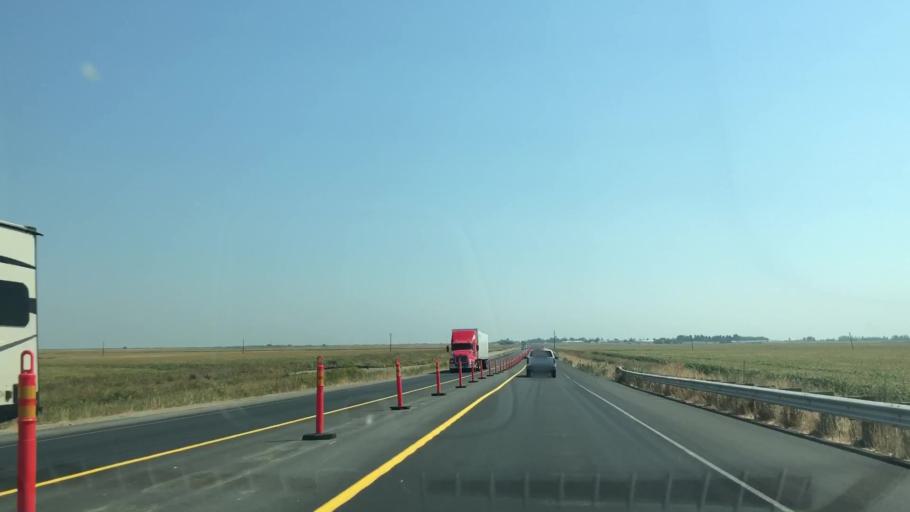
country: US
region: California
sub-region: Sacramento County
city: Walnut Grove
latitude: 38.1133
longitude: -121.5333
